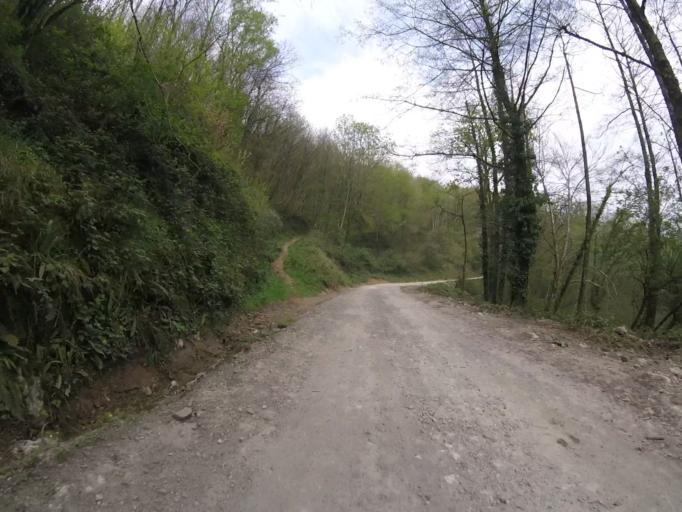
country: ES
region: Basque Country
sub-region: Provincia de Guipuzcoa
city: Asteasu
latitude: 43.2207
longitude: -2.0940
